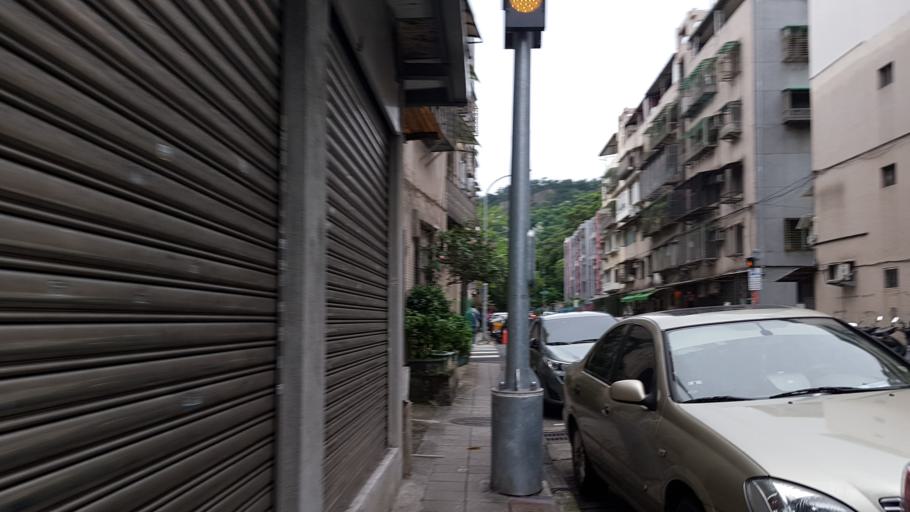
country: TW
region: Taipei
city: Taipei
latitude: 25.0181
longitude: 121.5569
